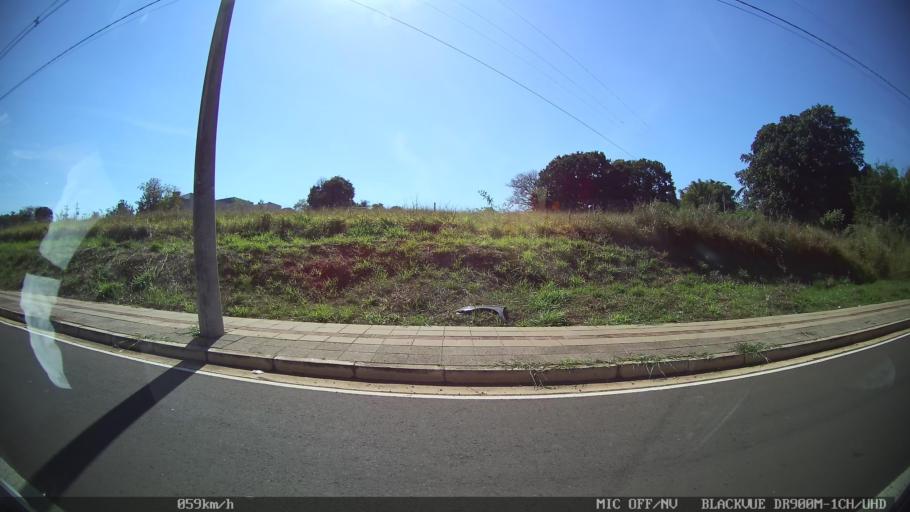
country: BR
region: Sao Paulo
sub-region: Sao Jose Do Rio Preto
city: Sao Jose do Rio Preto
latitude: -20.7778
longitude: -49.3841
